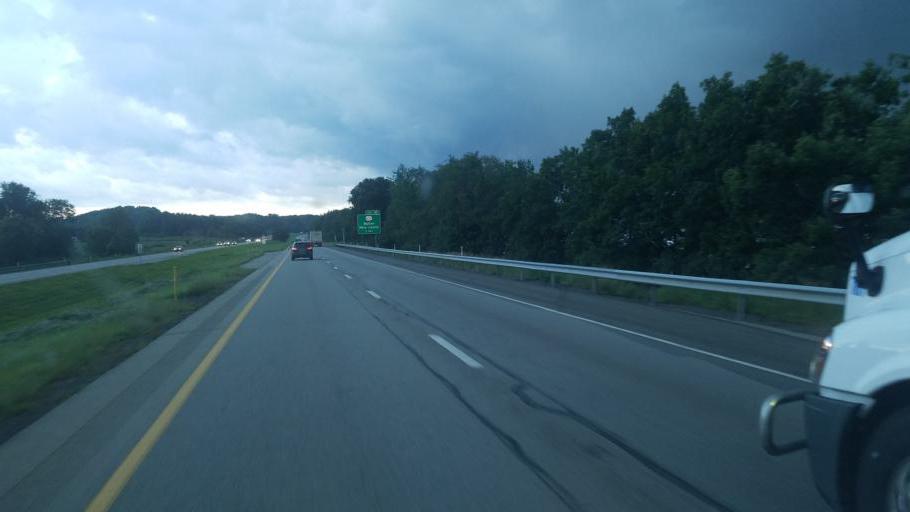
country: US
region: Pennsylvania
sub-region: Butler County
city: Prospect
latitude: 40.9782
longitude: -80.1332
